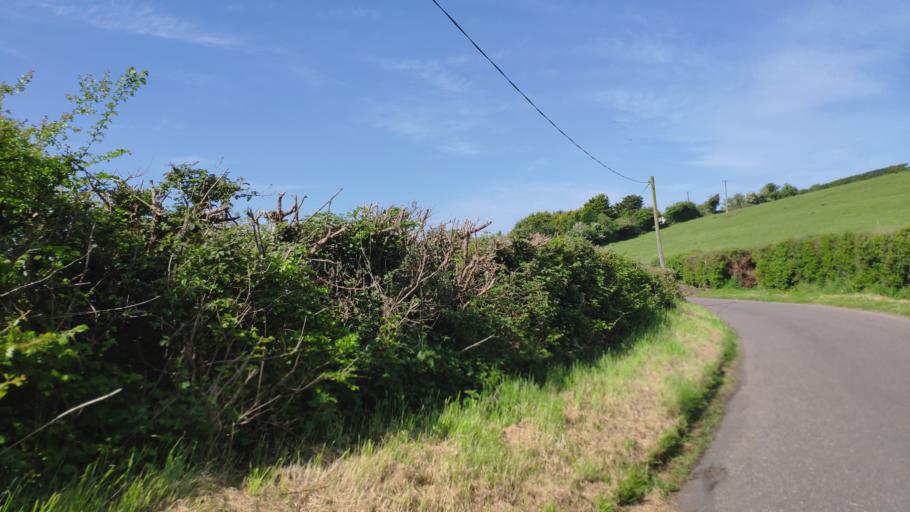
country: IE
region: Munster
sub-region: County Cork
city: Cork
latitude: 51.9176
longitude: -8.5125
